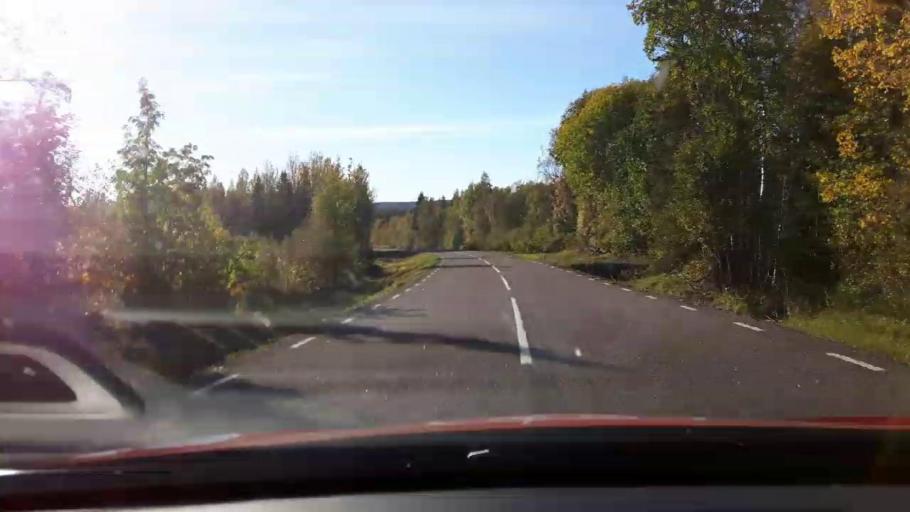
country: SE
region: Jaemtland
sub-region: Stroemsunds Kommun
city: Stroemsund
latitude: 63.8671
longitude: 15.1197
